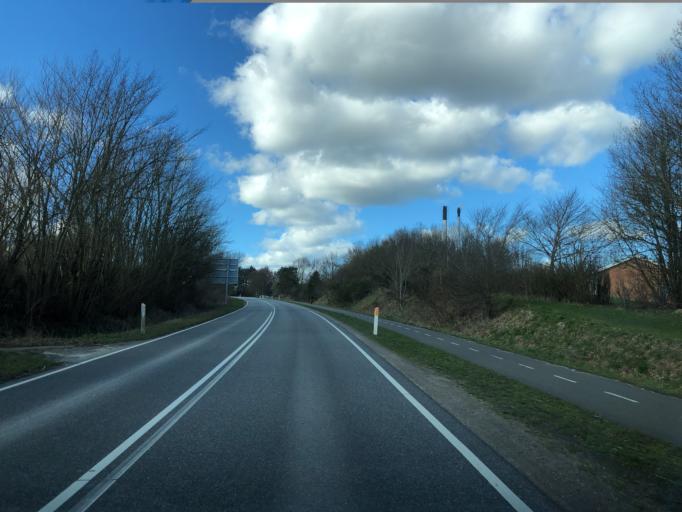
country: DK
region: Central Jutland
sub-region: Favrskov Kommune
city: Hinnerup
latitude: 56.2729
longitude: 10.0502
